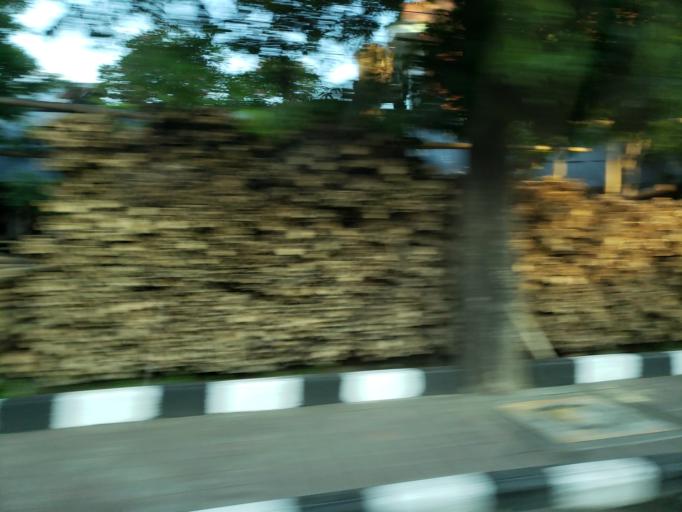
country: ID
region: Bali
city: Kelanabian
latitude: -8.7644
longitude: 115.1786
